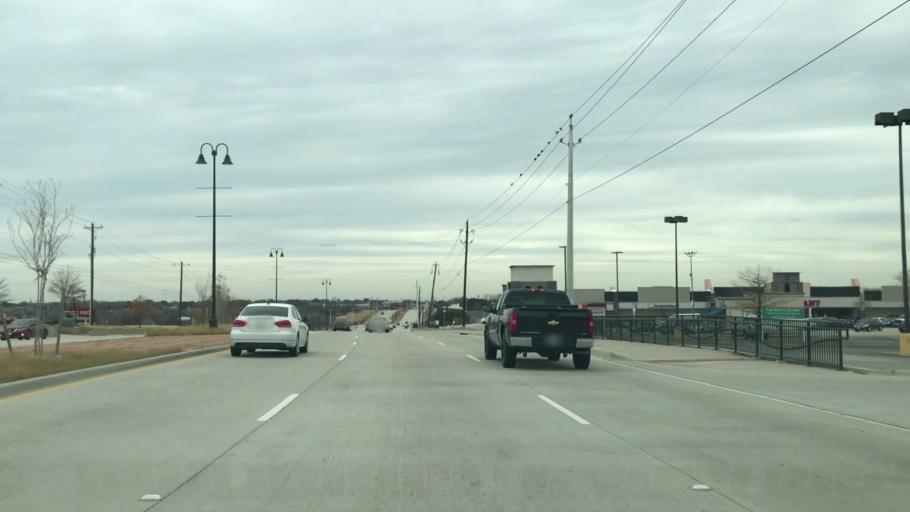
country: US
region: Texas
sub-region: Denton County
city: The Colony
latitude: 33.0813
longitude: -96.8926
